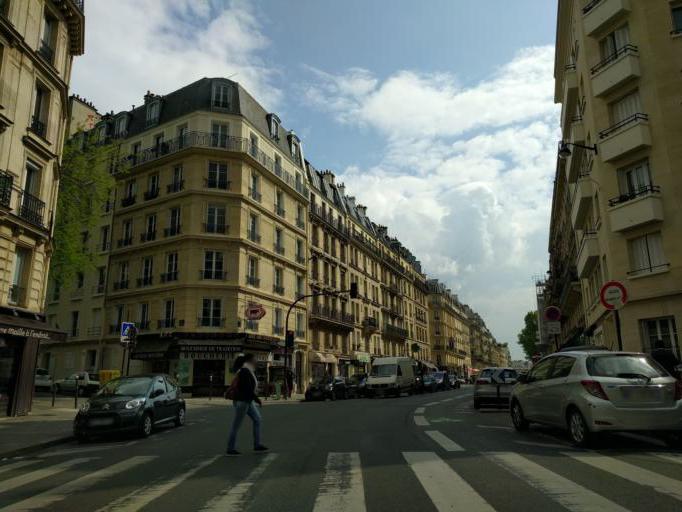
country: FR
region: Ile-de-France
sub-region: Paris
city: Paris
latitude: 48.8446
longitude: 2.3523
